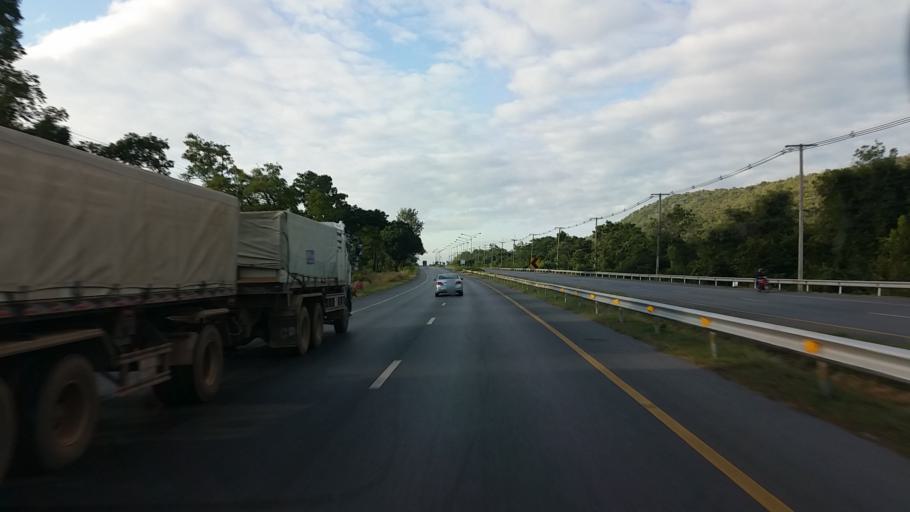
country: TH
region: Lop Buri
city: Phatthana Nikhom
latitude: 14.9746
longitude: 100.9040
